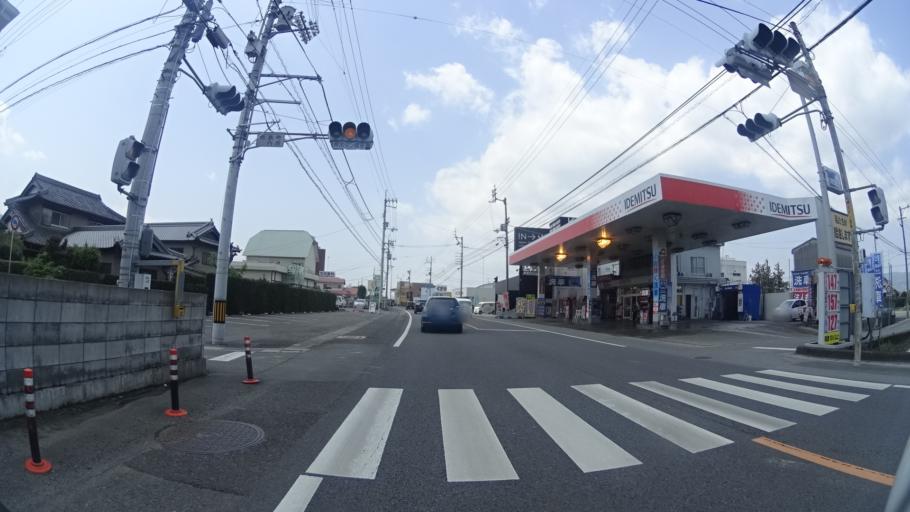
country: JP
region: Tokushima
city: Kamojimacho-jogejima
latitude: 34.0707
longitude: 134.3700
